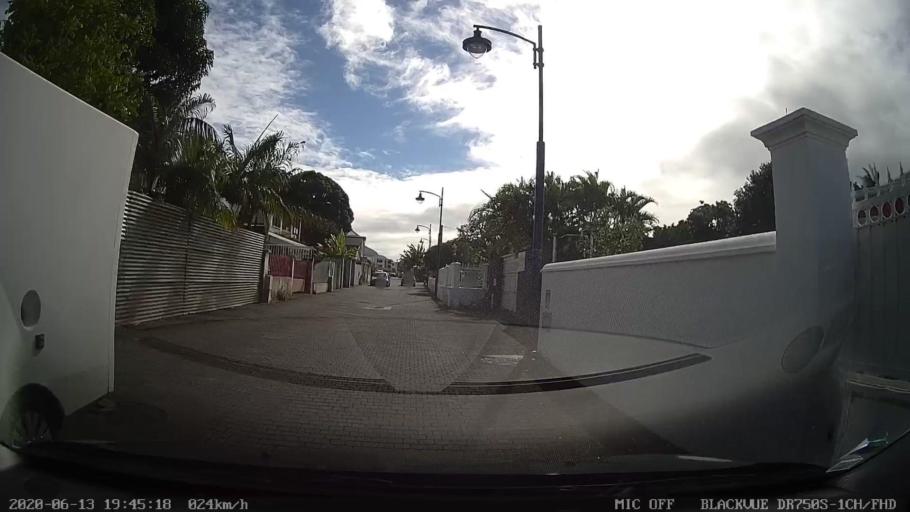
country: RE
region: Reunion
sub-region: Reunion
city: Bras-Panon
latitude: -20.9978
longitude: 55.6769
